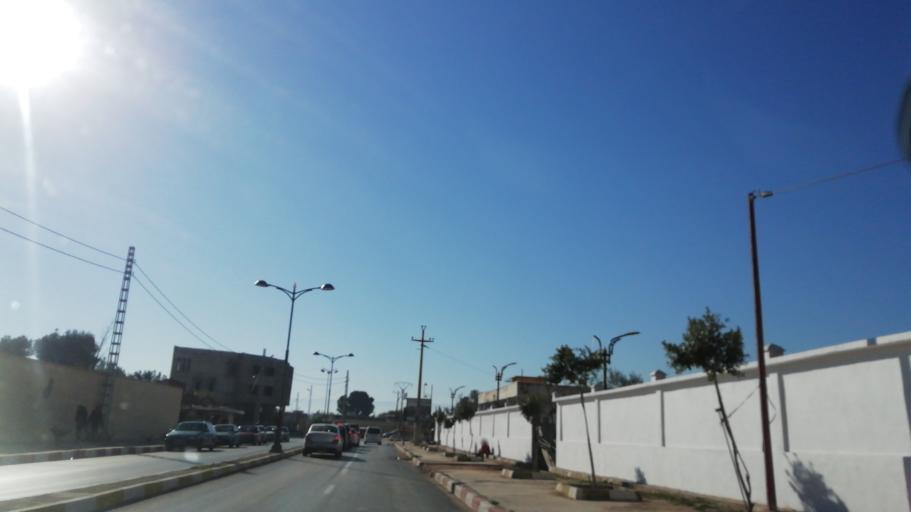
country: DZ
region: Tlemcen
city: Nedroma
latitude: 34.8469
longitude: -1.7396
